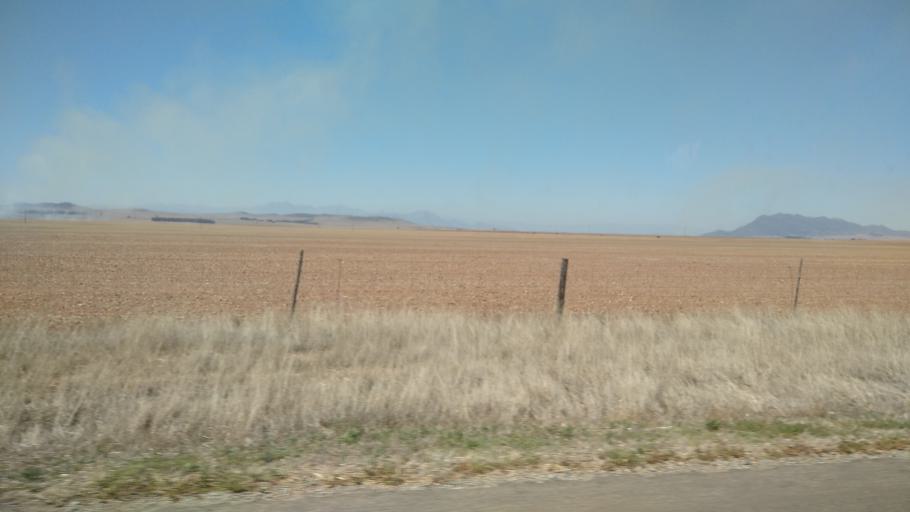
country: ZA
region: Western Cape
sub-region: West Coast District Municipality
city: Moorreesburg
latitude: -33.3106
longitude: 18.6200
